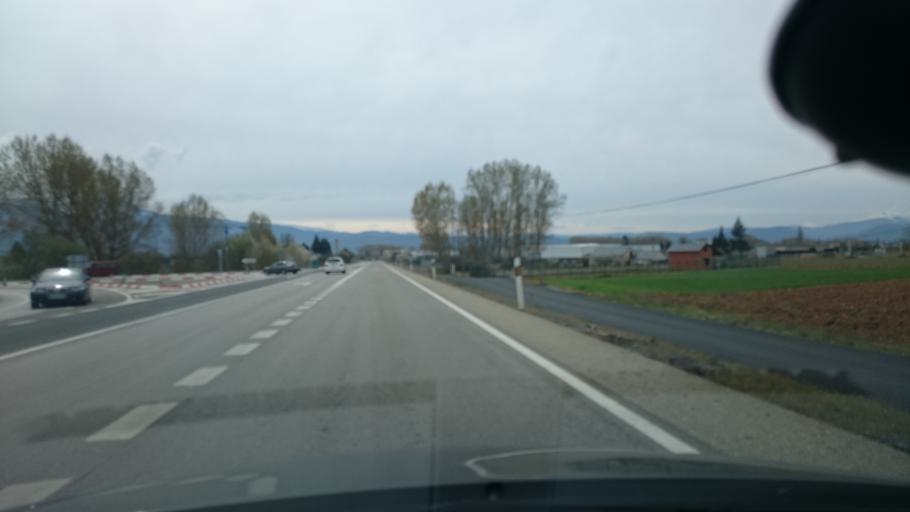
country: ES
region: Castille and Leon
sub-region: Provincia de Leon
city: Camponaraya
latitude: 42.5601
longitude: -6.6528
